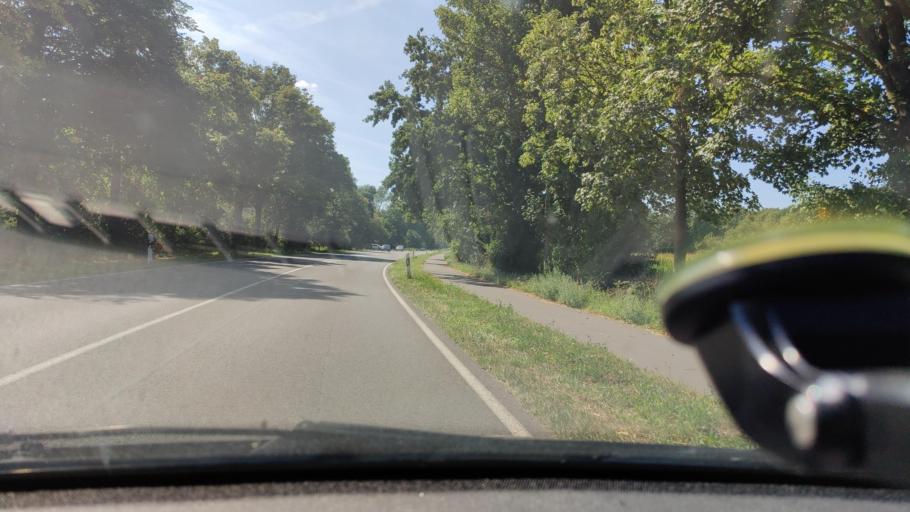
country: DE
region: North Rhine-Westphalia
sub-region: Regierungsbezirk Dusseldorf
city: Hunxe
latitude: 51.6458
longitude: 6.7807
